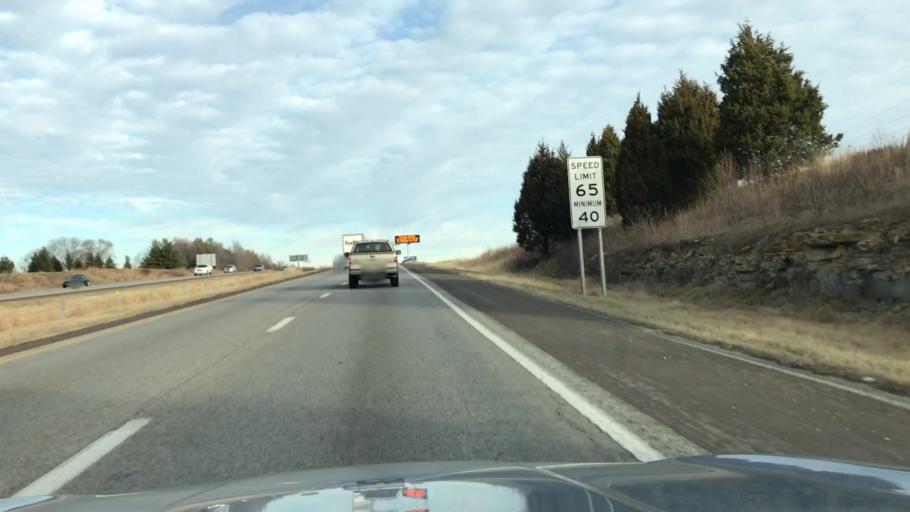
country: US
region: Missouri
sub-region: Jackson County
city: Blue Springs
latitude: 38.9916
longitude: -94.3574
